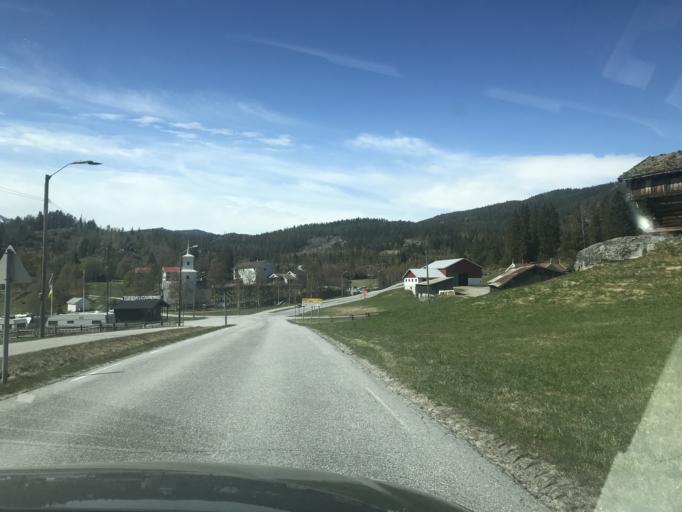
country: NO
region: Telemark
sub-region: Hjartdal
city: Sauland
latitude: 59.7552
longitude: 8.7919
